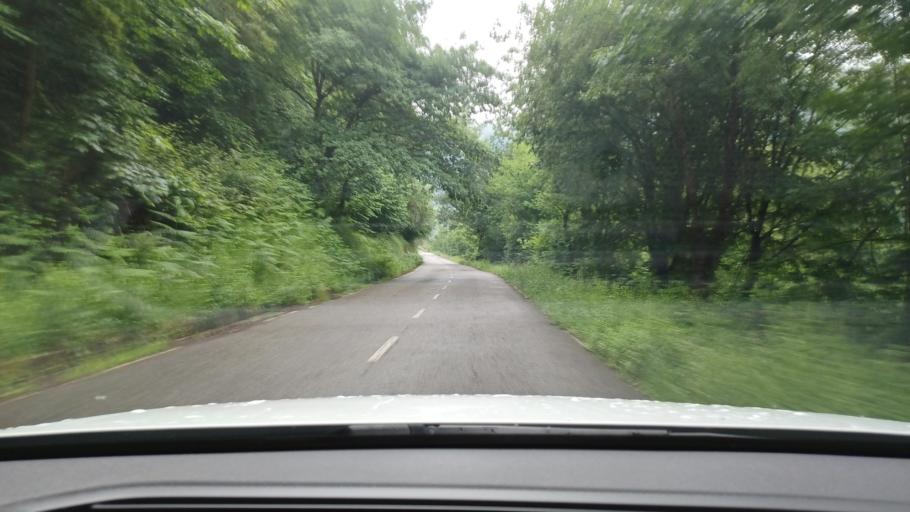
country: ES
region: Asturias
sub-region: Province of Asturias
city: Proaza
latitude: 43.2855
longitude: -5.9809
